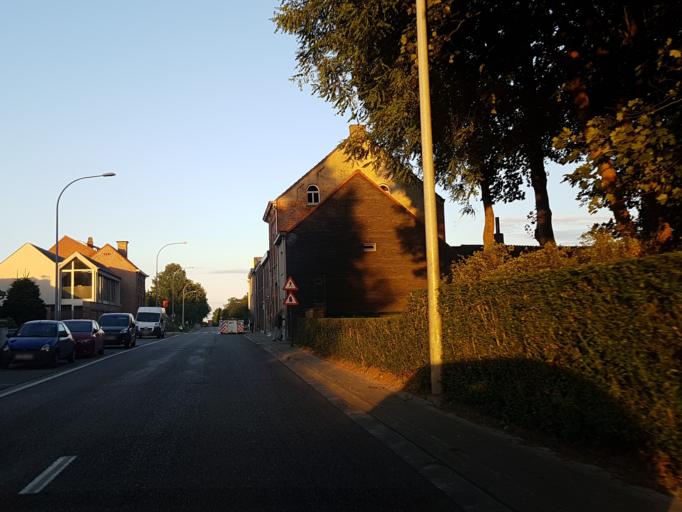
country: BE
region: Flanders
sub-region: Provincie Oost-Vlaanderen
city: Hamme
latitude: 51.1142
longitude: 4.1685
